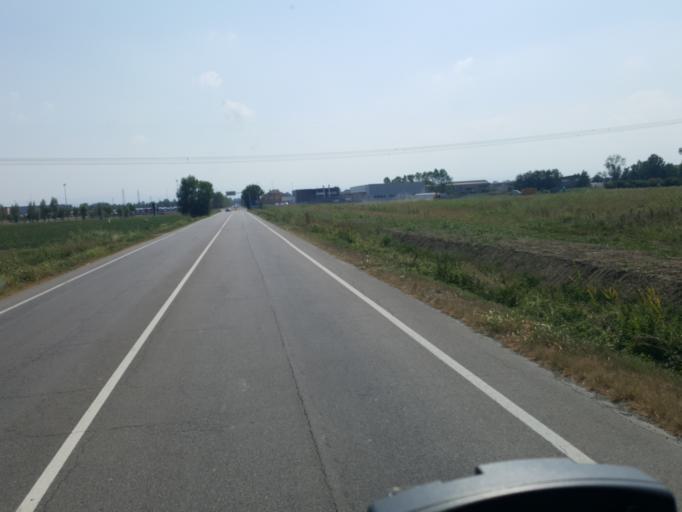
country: IT
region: Emilia-Romagna
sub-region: Provincia di Piacenza
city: Caorso
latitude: 45.0651
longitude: 9.8865
